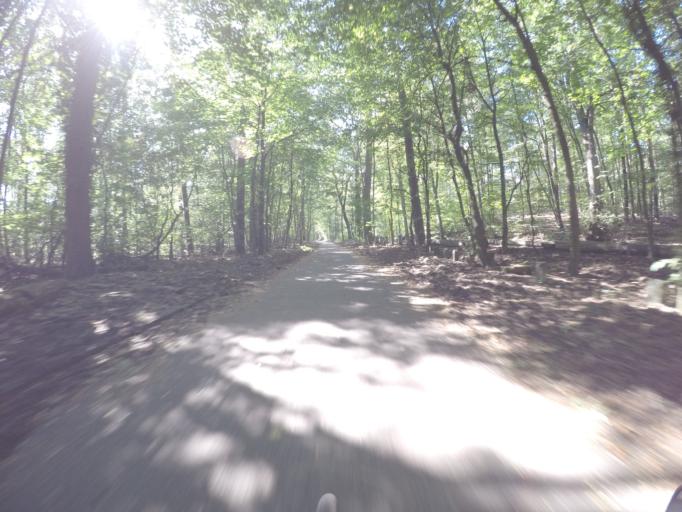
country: DE
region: Berlin
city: Konradshohe
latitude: 52.5806
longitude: 13.2459
